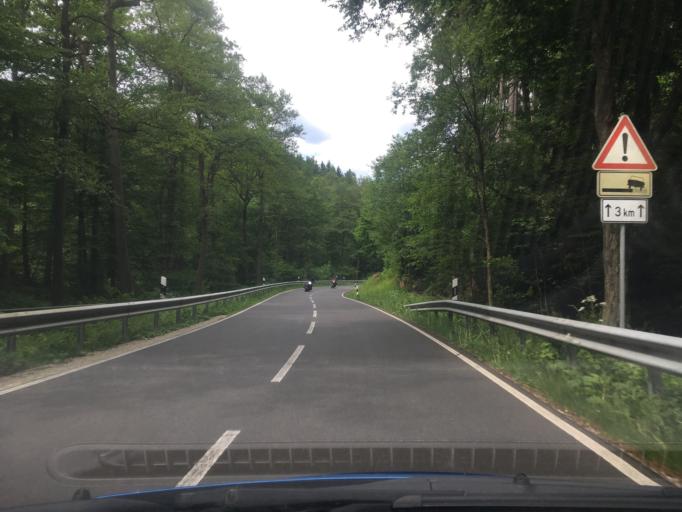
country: DE
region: Lower Saxony
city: Uslar
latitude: 51.7358
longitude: 9.6359
